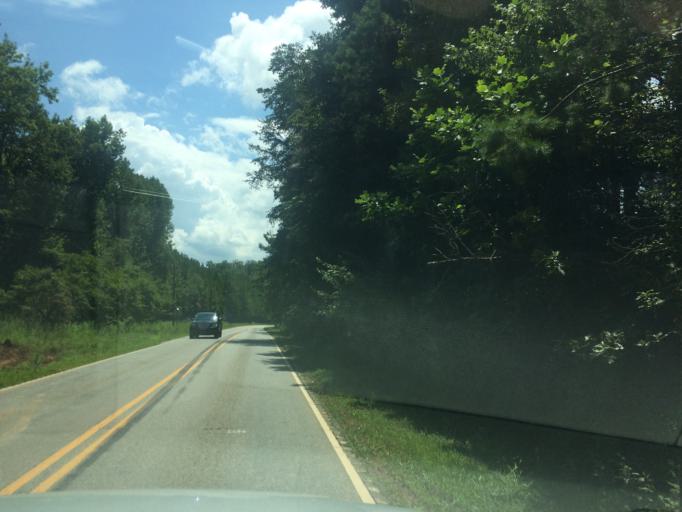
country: US
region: North Carolina
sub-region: Polk County
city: Columbus
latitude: 35.3096
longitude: -82.1666
